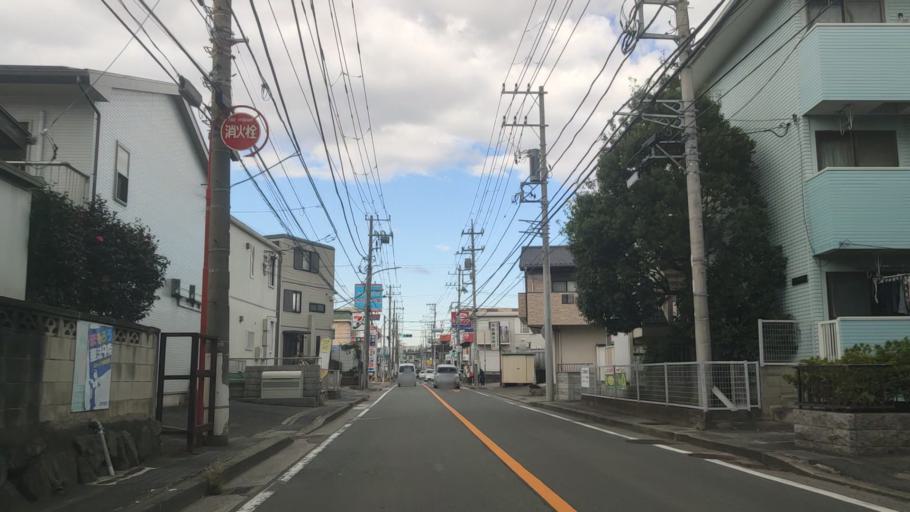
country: JP
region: Kanagawa
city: Fujisawa
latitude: 35.4228
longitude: 139.5324
